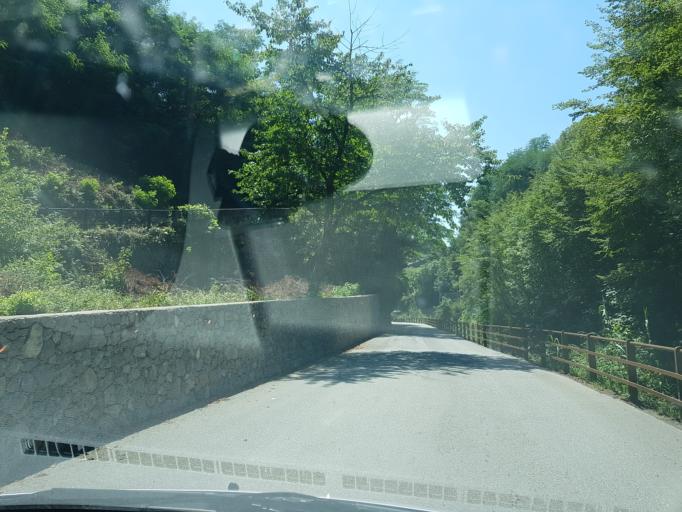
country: IT
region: Liguria
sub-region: Provincia di Genova
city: San Teodoro
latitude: 44.4462
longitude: 8.8539
